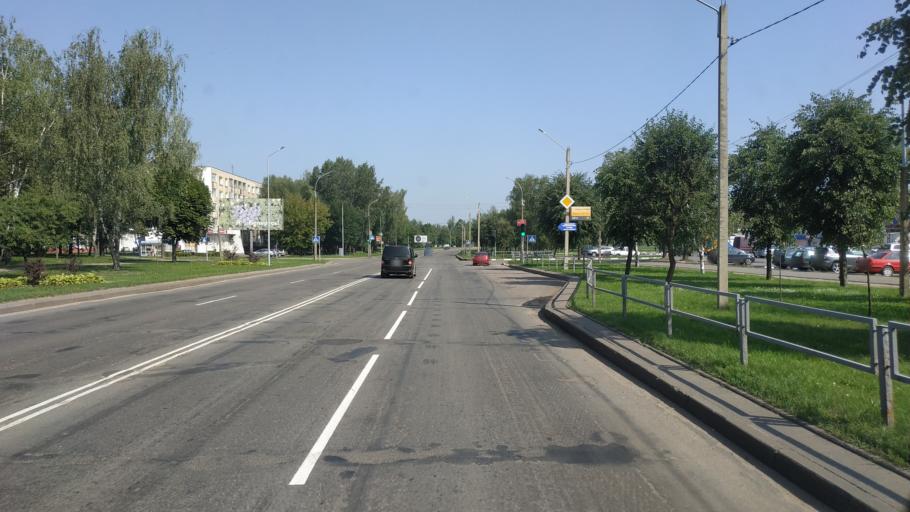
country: BY
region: Mogilev
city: Buynichy
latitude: 53.8724
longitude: 30.3129
